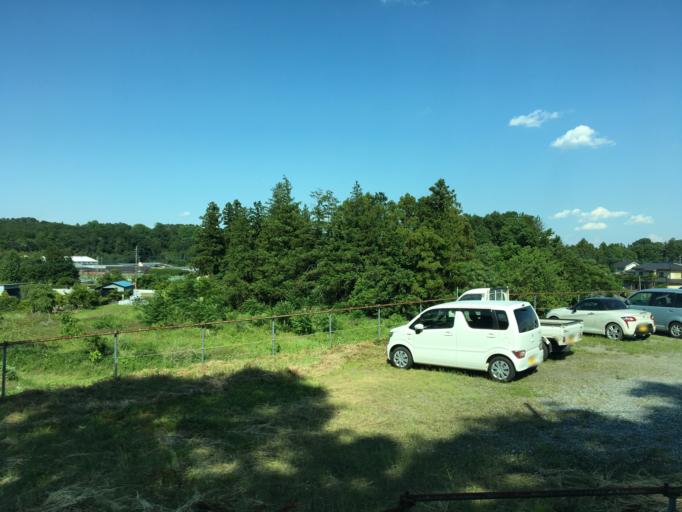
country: JP
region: Saitama
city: Morohongo
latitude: 35.9809
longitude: 139.3345
